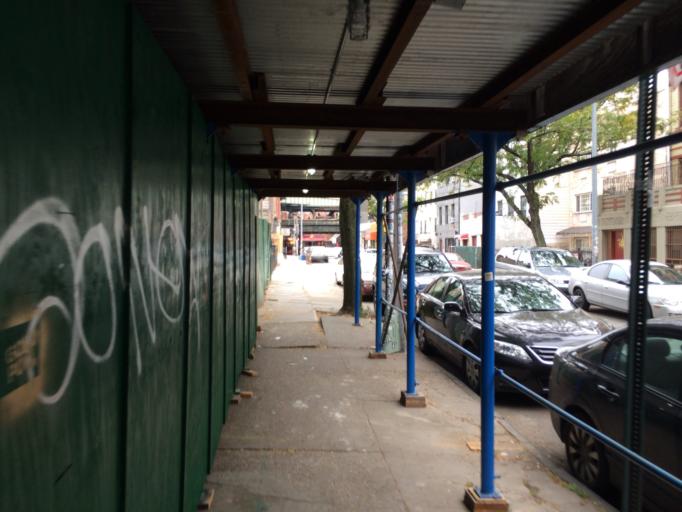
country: US
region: New York
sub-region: Queens County
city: Long Island City
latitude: 40.6980
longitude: -73.9342
